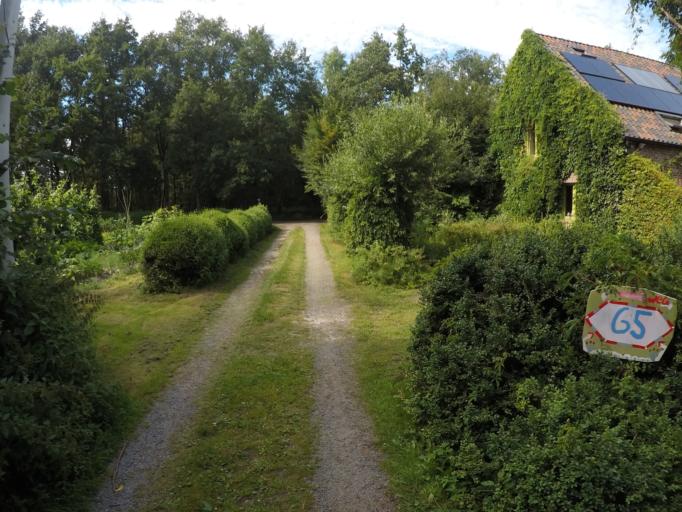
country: BE
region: Flanders
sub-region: Provincie Antwerpen
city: Berlaar
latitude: 51.1450
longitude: 4.6427
